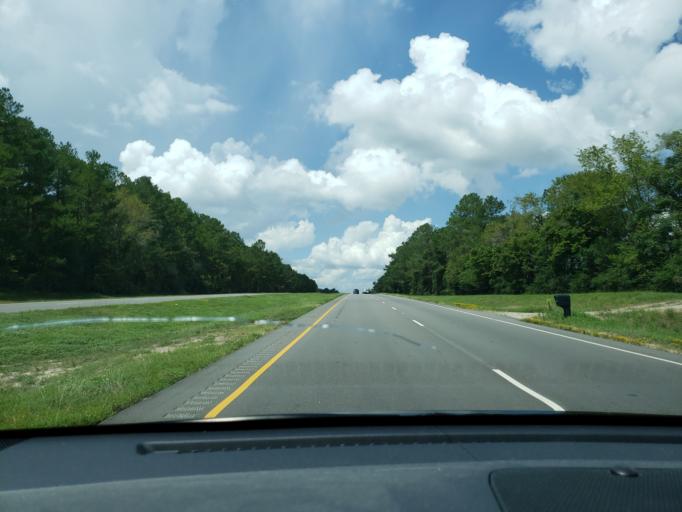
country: US
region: North Carolina
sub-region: Robeson County
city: Saint Pauls
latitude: 34.8161
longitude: -78.8389
